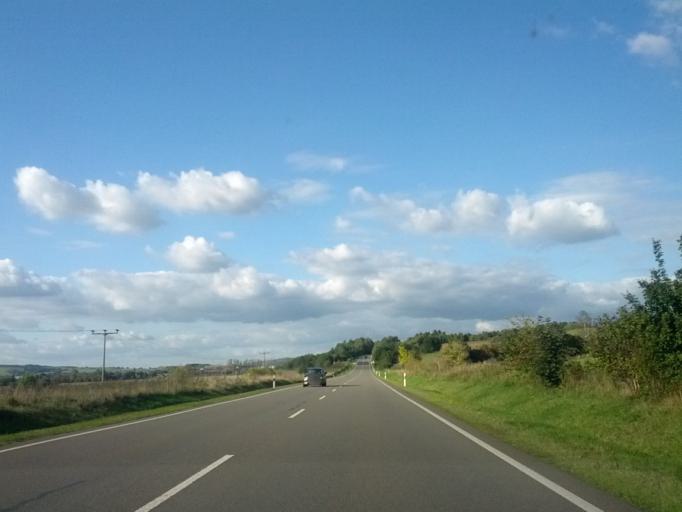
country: DE
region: Thuringia
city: Breitungen
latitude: 50.7799
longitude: 10.3172
